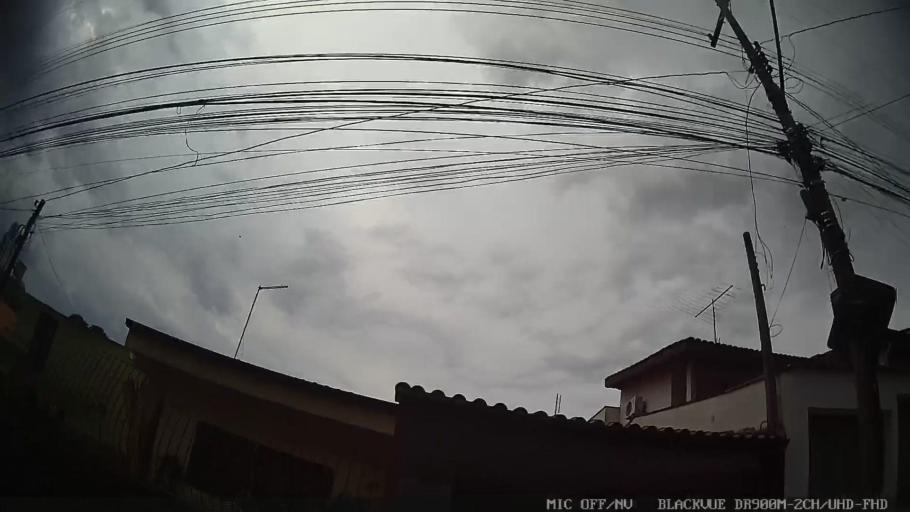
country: BR
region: Sao Paulo
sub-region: Itatiba
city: Itatiba
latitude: -23.0090
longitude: -46.8345
